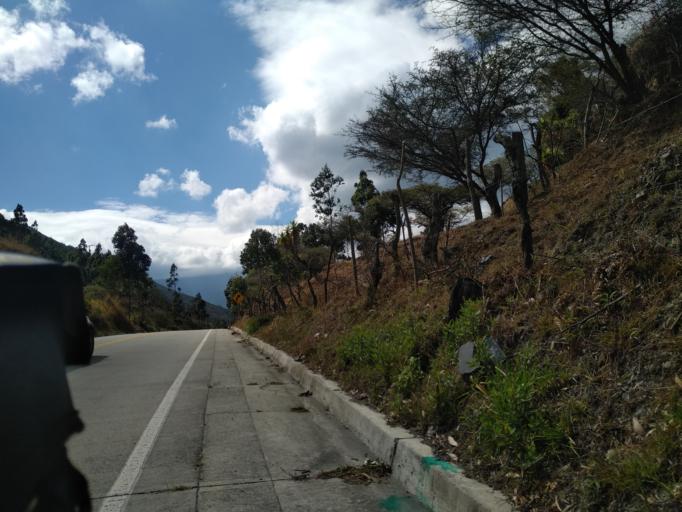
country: EC
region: Loja
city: Loja
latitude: -4.3481
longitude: -79.1908
